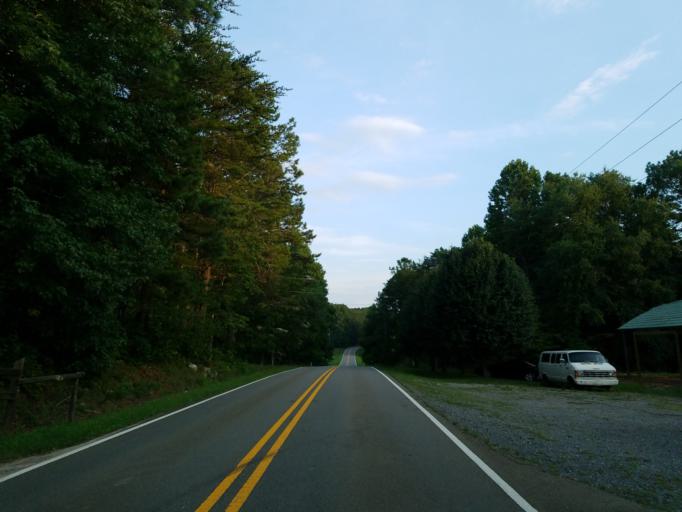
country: US
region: Georgia
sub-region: Pickens County
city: Jasper
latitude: 34.5550
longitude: -84.4698
